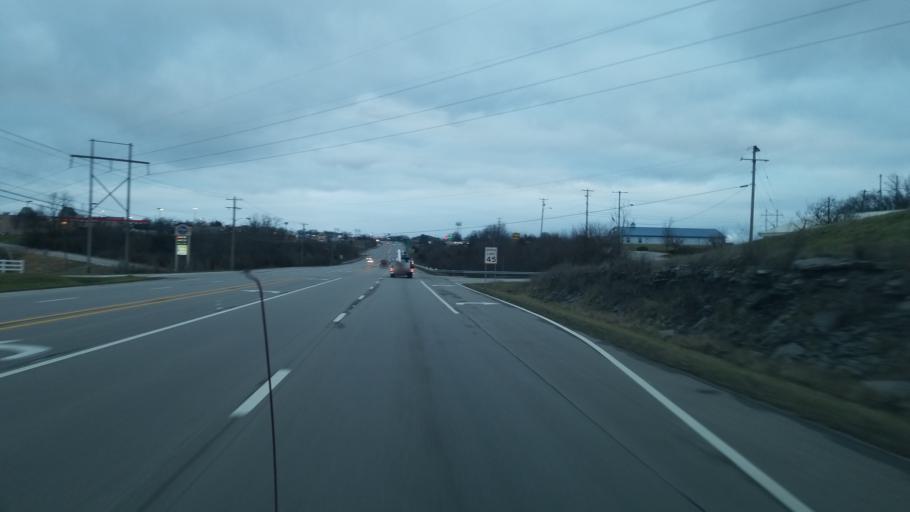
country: US
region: Ohio
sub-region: Brown County
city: Aberdeen
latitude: 38.6244
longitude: -83.7870
